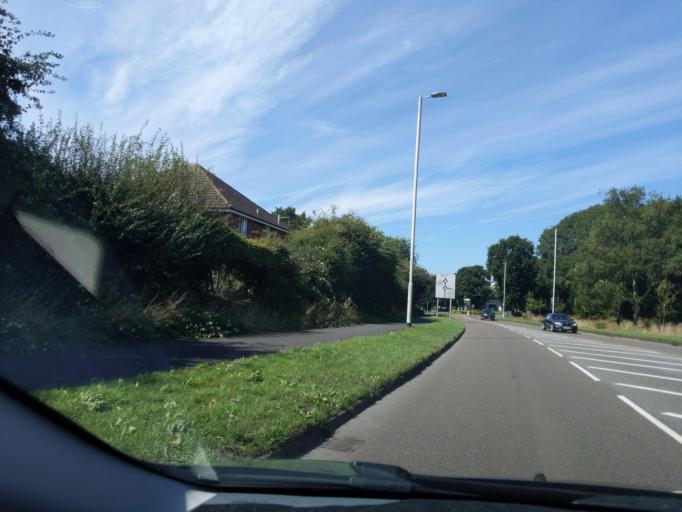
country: GB
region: England
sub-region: Devon
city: Plympton
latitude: 50.3913
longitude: -4.0460
